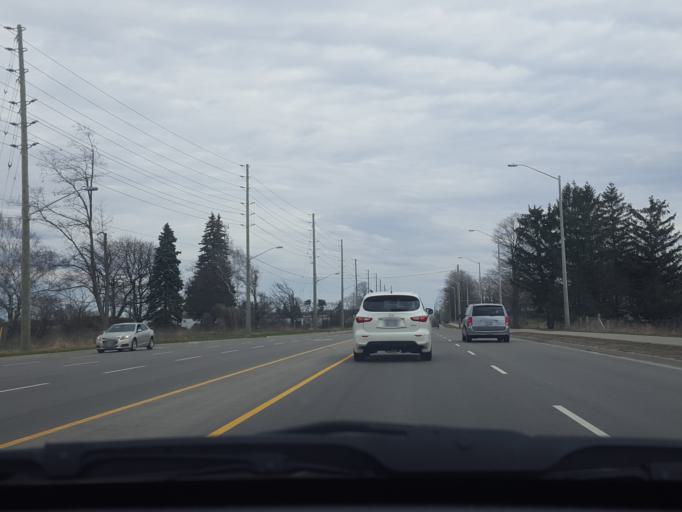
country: CA
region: Ontario
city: Ajax
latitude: 43.8506
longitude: -78.9880
